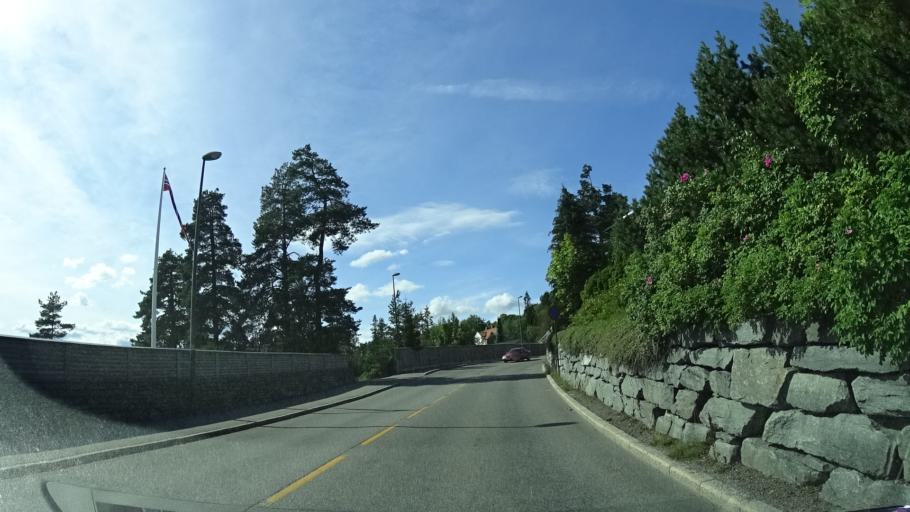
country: NO
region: Oslo
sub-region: Oslo
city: Sjolyststranda
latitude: 59.9584
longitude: 10.6717
